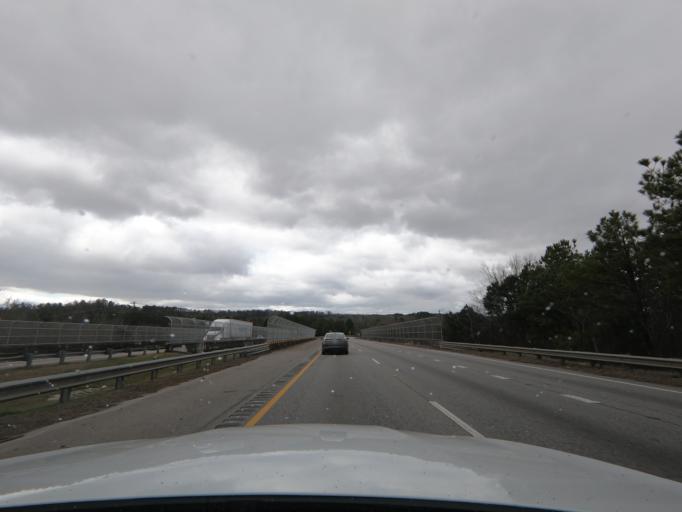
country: US
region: Alabama
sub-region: Russell County
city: Phenix City
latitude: 32.4905
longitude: -85.0300
